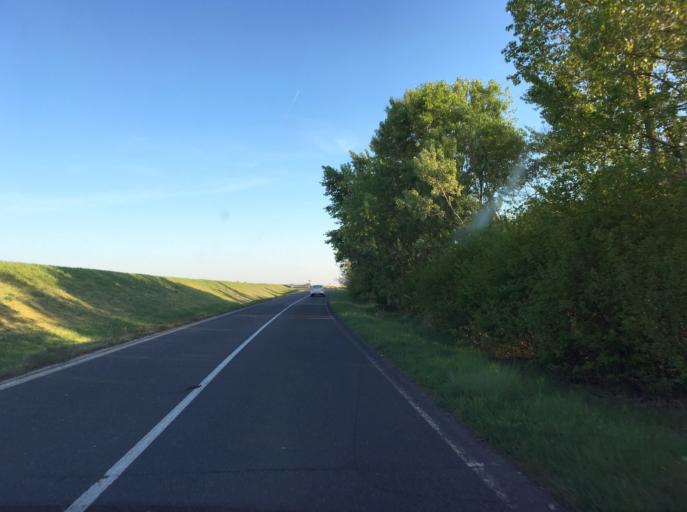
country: HU
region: Gyor-Moson-Sopron
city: Rajka
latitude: 48.0191
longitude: 17.2502
